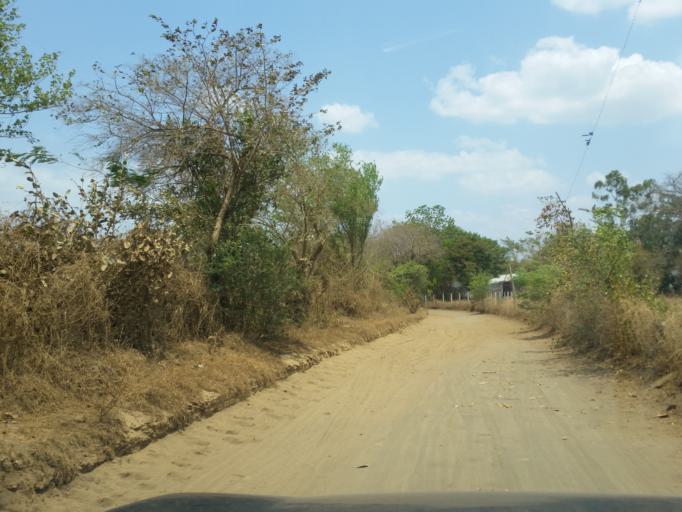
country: NI
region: Managua
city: Managua
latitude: 12.1258
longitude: -86.1625
